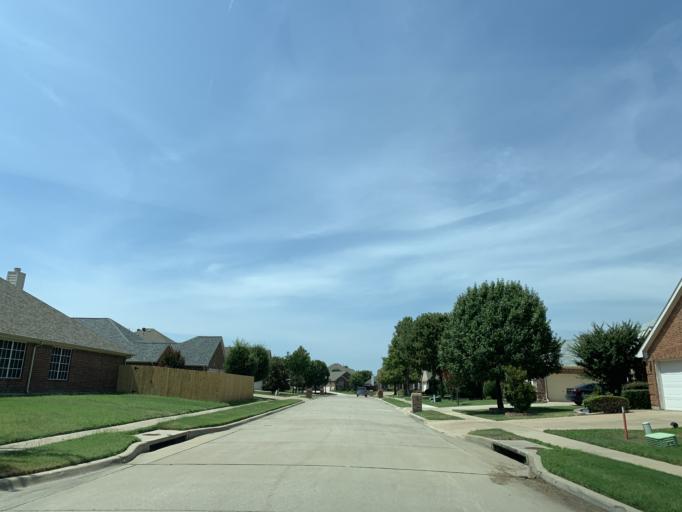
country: US
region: Texas
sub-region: Dallas County
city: Cedar Hill
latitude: 32.6442
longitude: -97.0402
